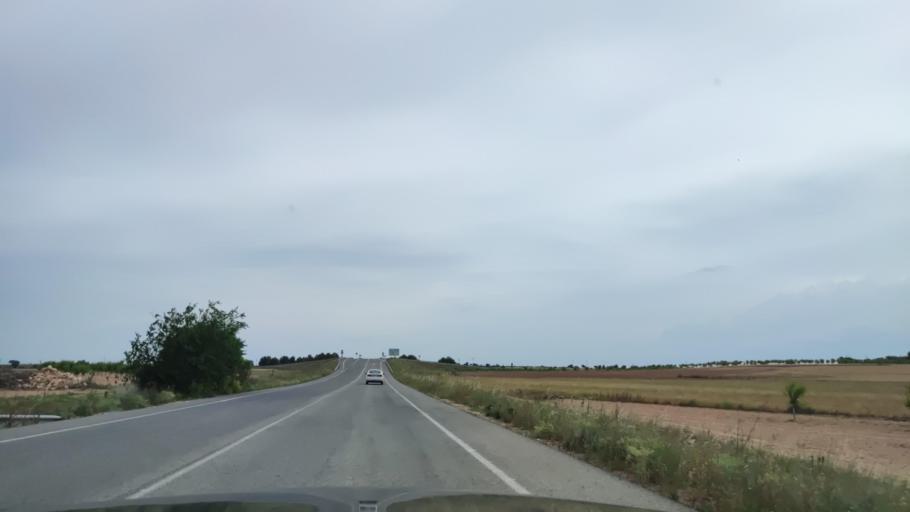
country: ES
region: Castille-La Mancha
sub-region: Provincia de Albacete
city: La Roda
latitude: 39.2239
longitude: -2.1892
